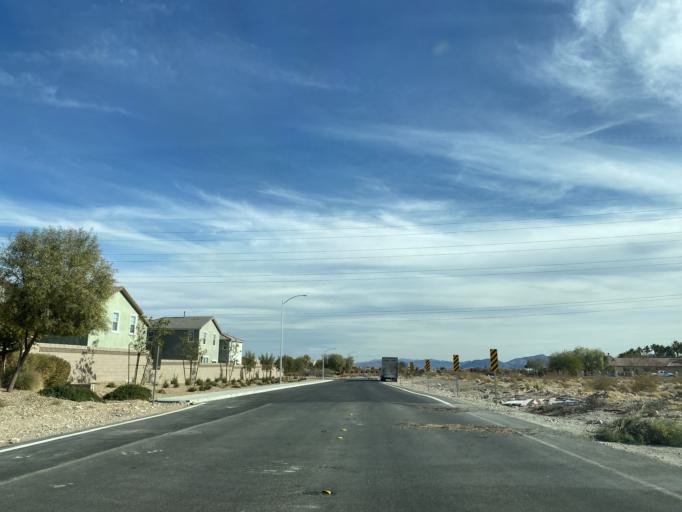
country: US
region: Nevada
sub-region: Clark County
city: Enterprise
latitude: 36.0406
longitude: -115.2138
